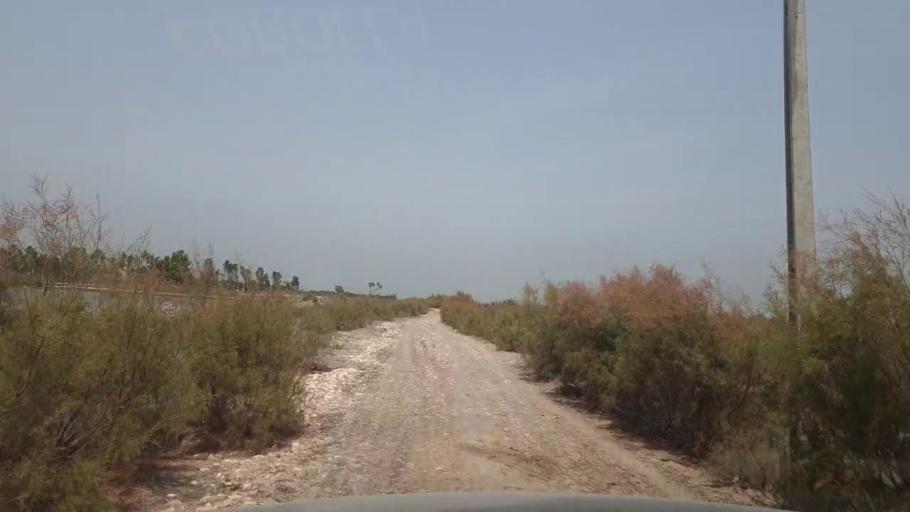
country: PK
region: Sindh
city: Garhi Yasin
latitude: 27.9198
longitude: 68.4142
